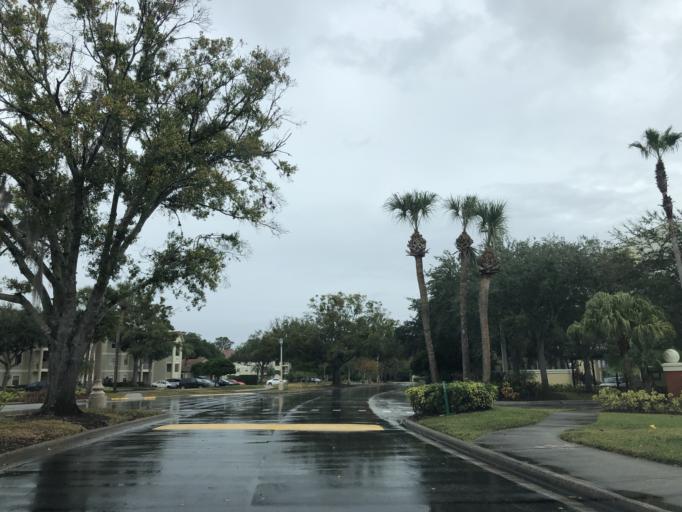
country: US
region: Florida
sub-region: Osceola County
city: Celebration
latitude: 28.3378
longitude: -81.5349
